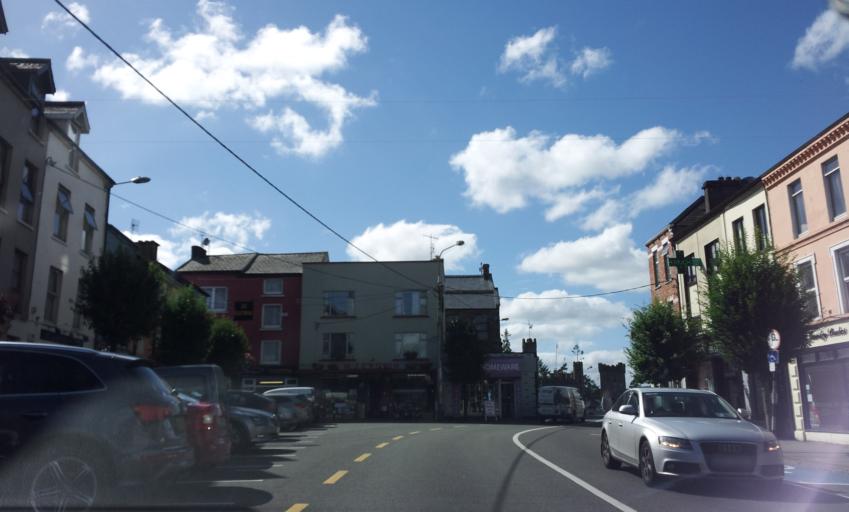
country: IE
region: Munster
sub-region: County Cork
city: Macroom
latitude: 51.9046
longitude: -8.9585
